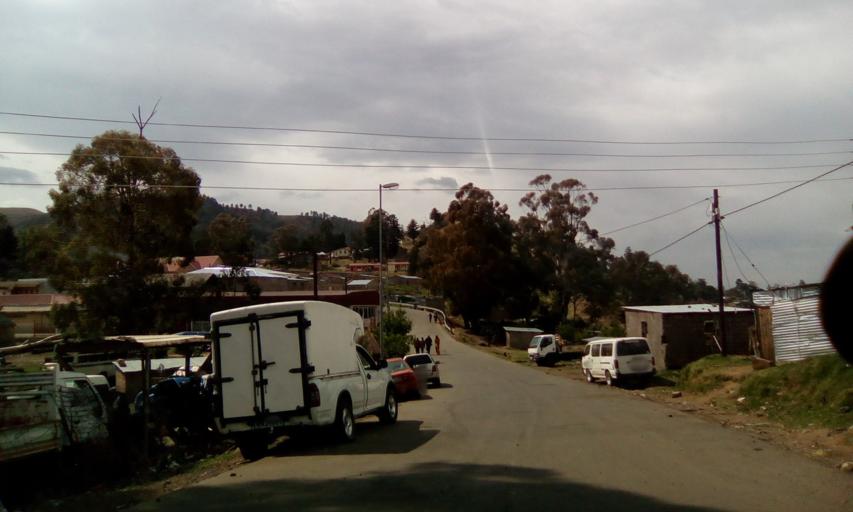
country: LS
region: Qacha's Nek
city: Qacha's Nek
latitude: -30.1184
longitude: 28.6835
